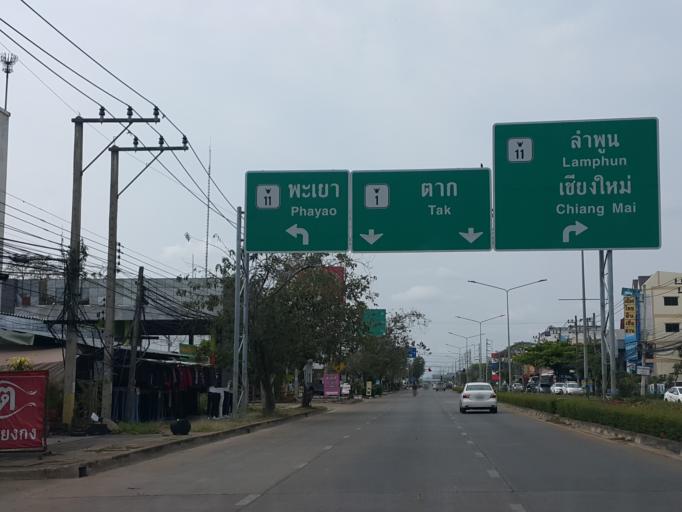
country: TH
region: Lampang
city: Lampang
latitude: 18.2694
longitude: 99.4675
